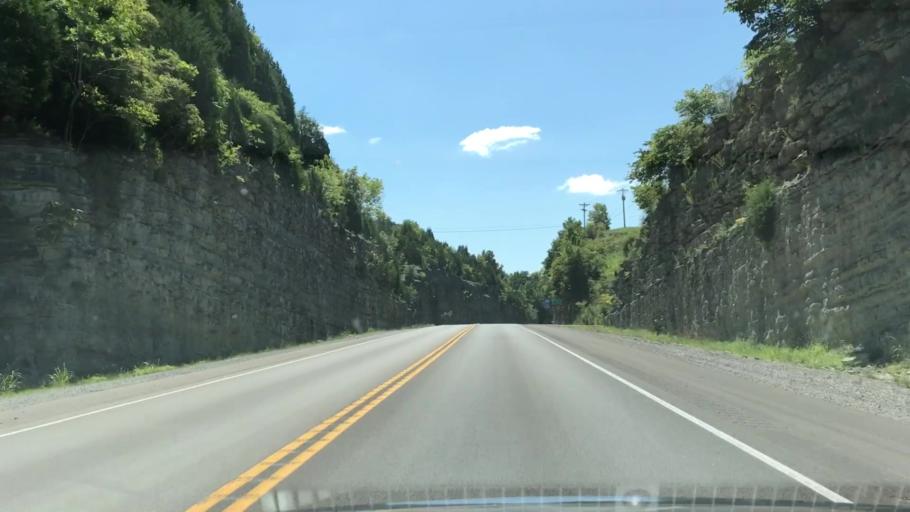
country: US
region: Kentucky
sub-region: Cumberland County
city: Burkesville
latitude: 36.7164
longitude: -85.3648
